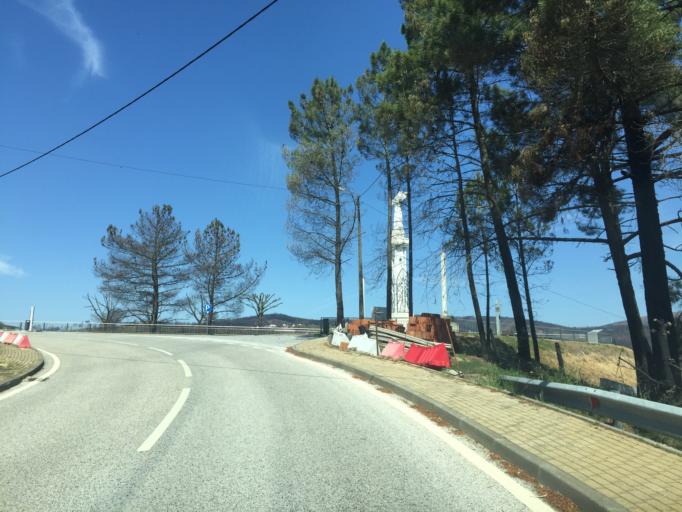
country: PT
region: Coimbra
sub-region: Pampilhosa da Serra
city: Pampilhosa da Serra
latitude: 40.0446
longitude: -7.9538
